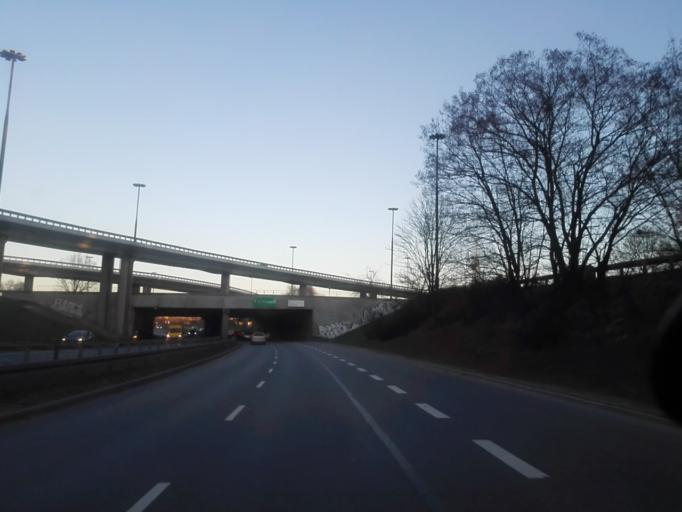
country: PL
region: Masovian Voivodeship
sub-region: Warszawa
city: Mokotow
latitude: 52.1669
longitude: 21.0159
